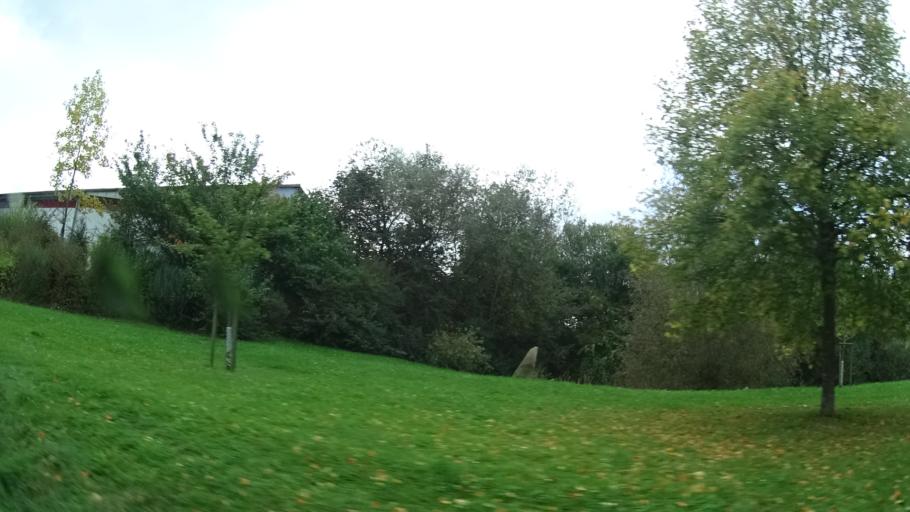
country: DE
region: Baden-Wuerttemberg
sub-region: Karlsruhe Region
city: Hardheim
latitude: 49.6187
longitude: 9.4756
